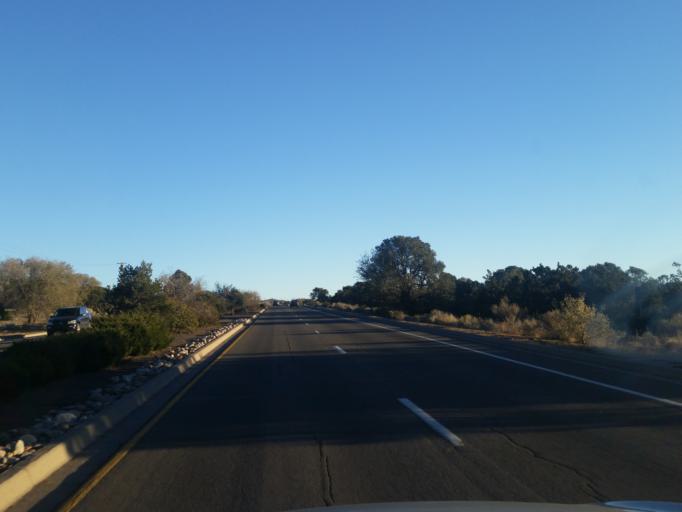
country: US
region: New Mexico
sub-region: Santa Fe County
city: Santa Fe
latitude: 35.6496
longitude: -105.9354
